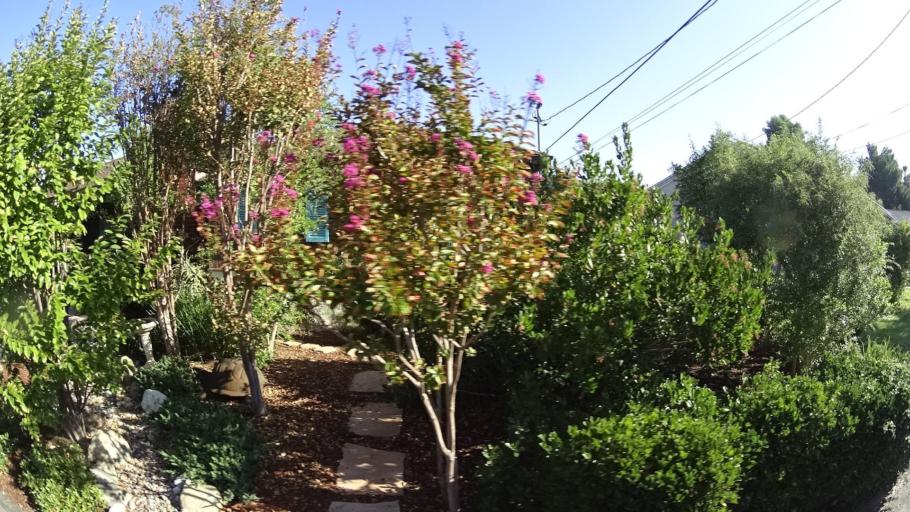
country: US
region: California
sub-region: San Diego County
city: Spring Valley
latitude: 32.7625
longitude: -116.9987
